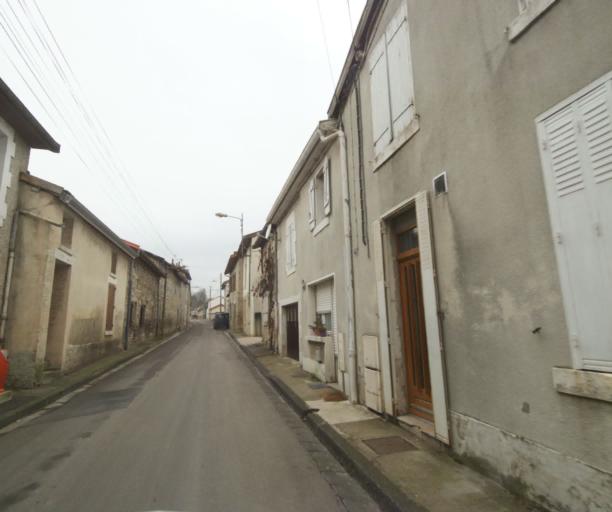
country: FR
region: Champagne-Ardenne
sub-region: Departement de la Haute-Marne
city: Bienville
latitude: 48.5830
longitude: 5.0387
